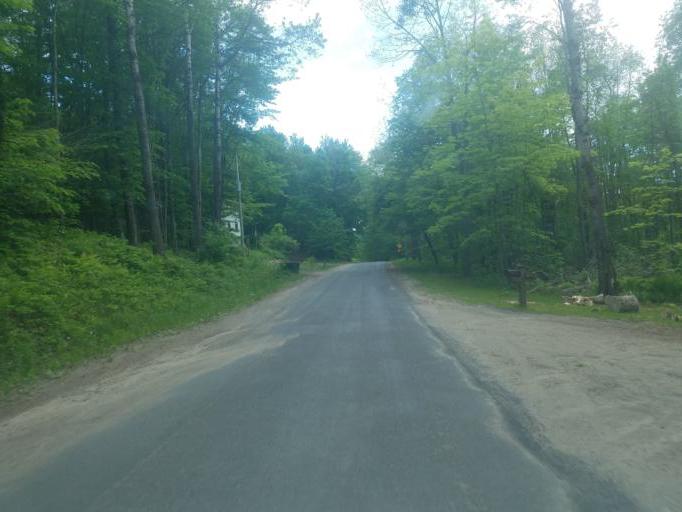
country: US
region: New York
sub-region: Herkimer County
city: Herkimer
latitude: 43.2266
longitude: -74.9652
